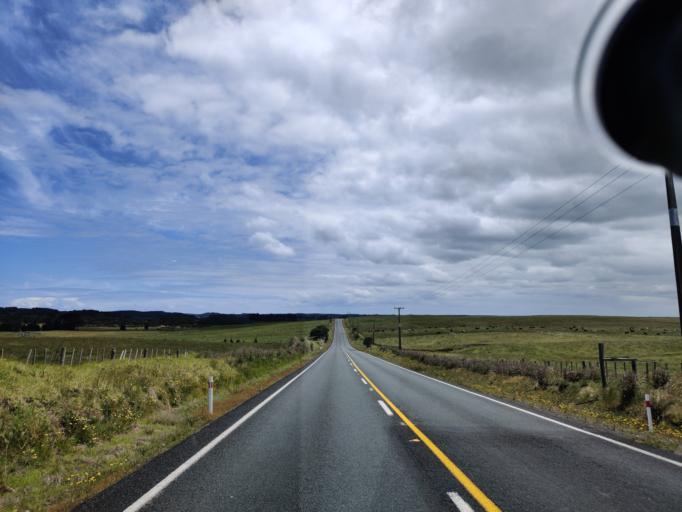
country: NZ
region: Northland
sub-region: Far North District
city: Kaitaia
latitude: -34.6902
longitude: 173.0183
